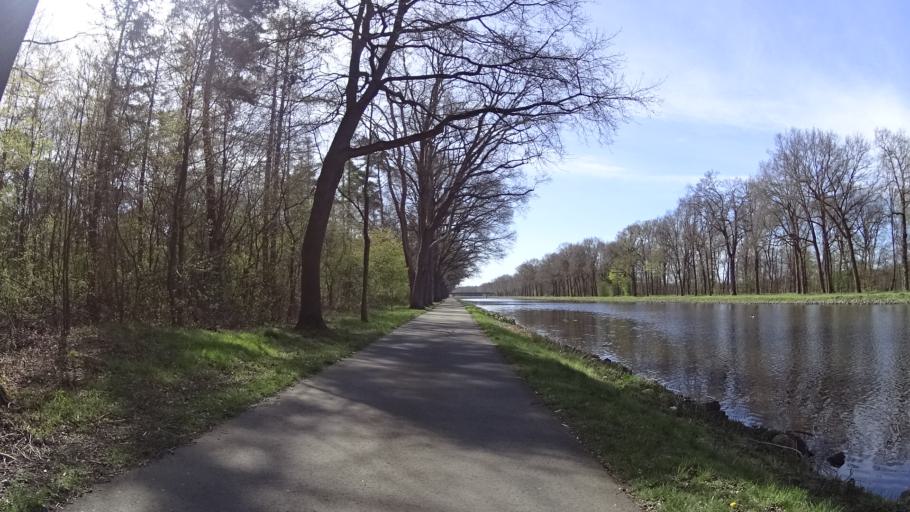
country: DE
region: Lower Saxony
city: Geeste
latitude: 52.6053
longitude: 7.3088
